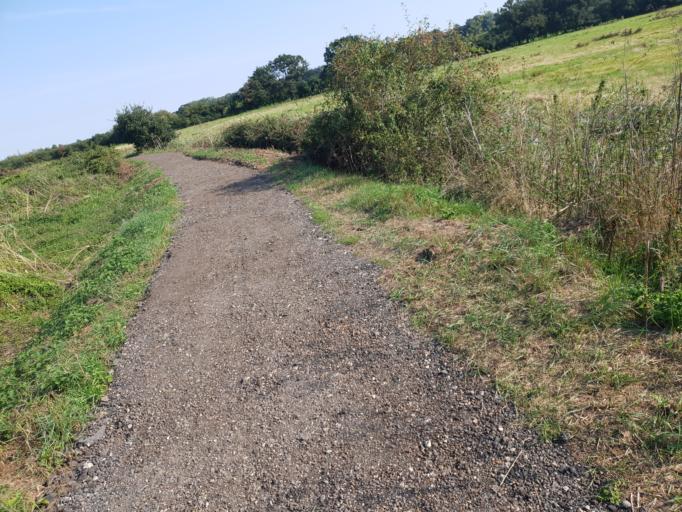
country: GB
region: England
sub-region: Suffolk
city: East Bergholt
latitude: 51.9531
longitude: 1.0287
